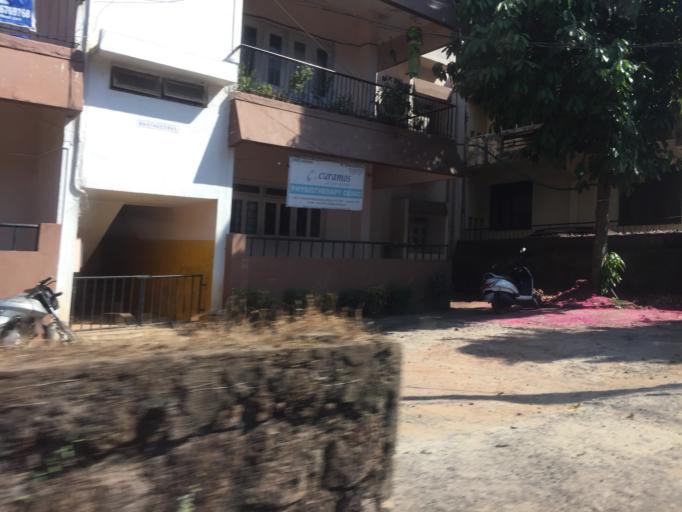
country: IN
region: Goa
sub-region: South Goa
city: Vasco Da Gama
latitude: 15.3937
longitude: 73.8182
